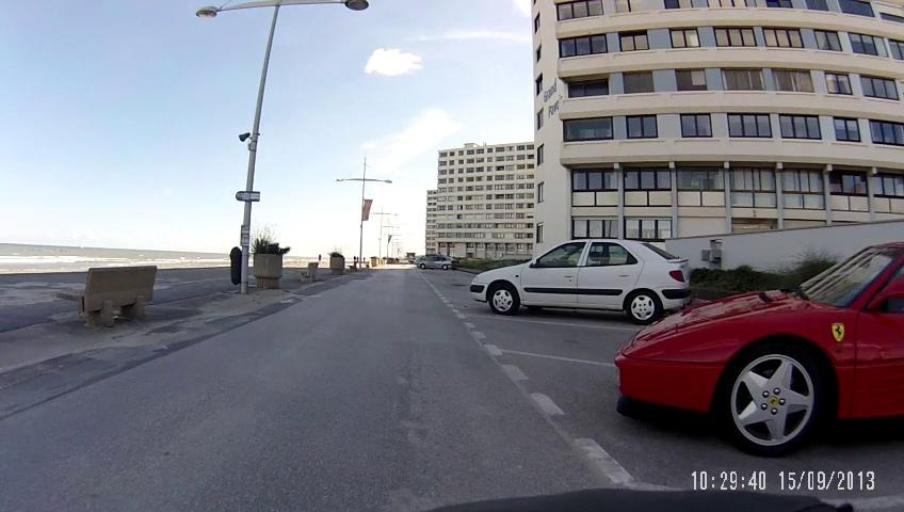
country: FR
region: Nord-Pas-de-Calais
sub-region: Departement du Nord
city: Coudekerque-Branche
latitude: 51.0526
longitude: 2.4086
